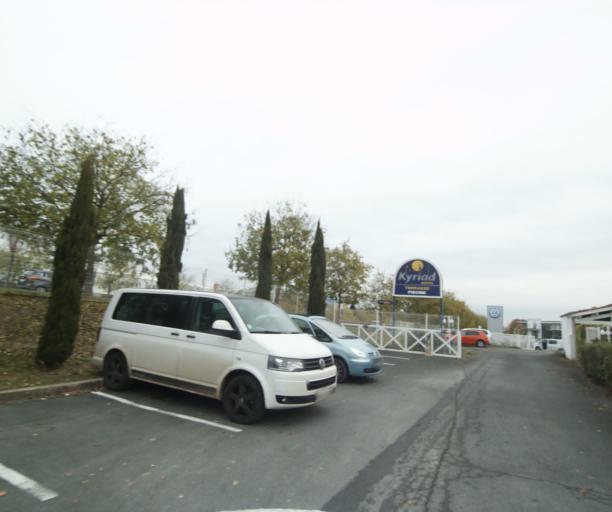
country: FR
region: Poitou-Charentes
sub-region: Departement de la Charente-Maritime
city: Saintes
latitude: 45.7402
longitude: -0.6650
